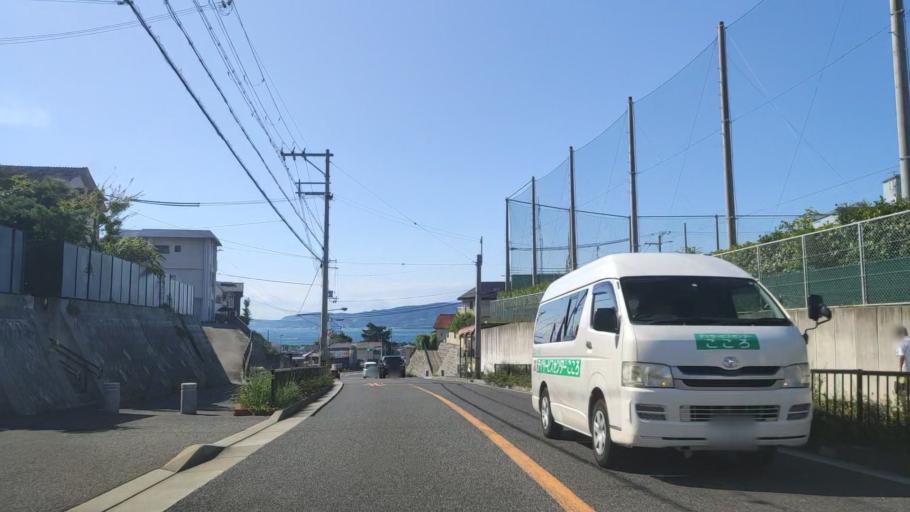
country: JP
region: Hyogo
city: Akashi
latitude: 34.6501
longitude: 135.0058
